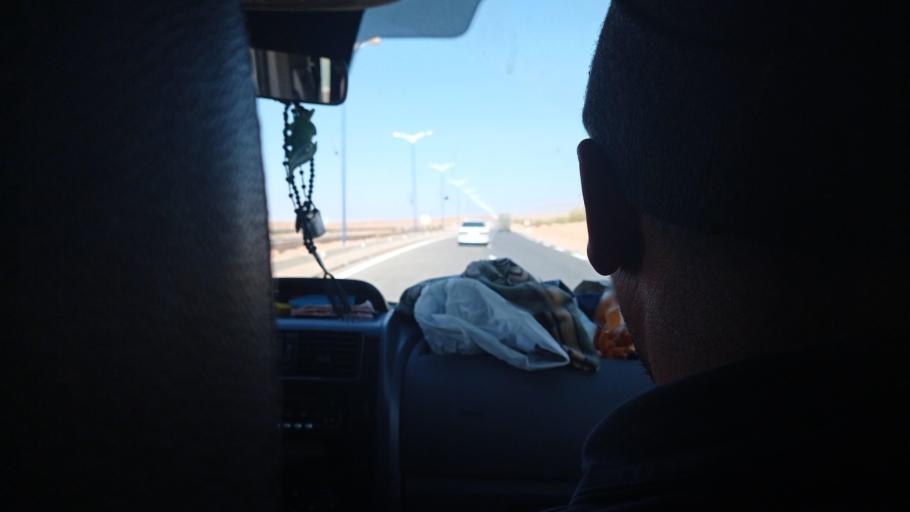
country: DZ
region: Wilaya de Naama
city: Ain Sefra
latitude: 32.7960
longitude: -0.6143
